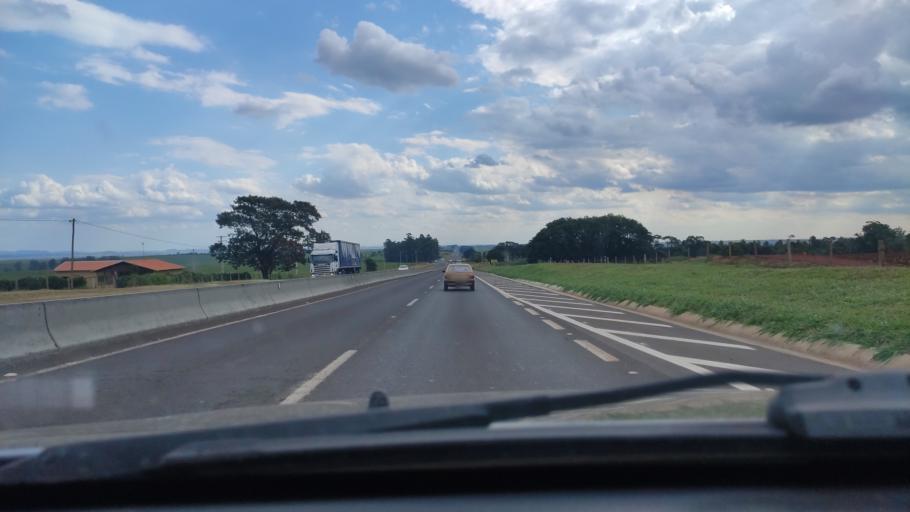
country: BR
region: Sao Paulo
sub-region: Santa Cruz Do Rio Pardo
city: Santa Cruz do Rio Pardo
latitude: -22.8821
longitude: -49.6922
